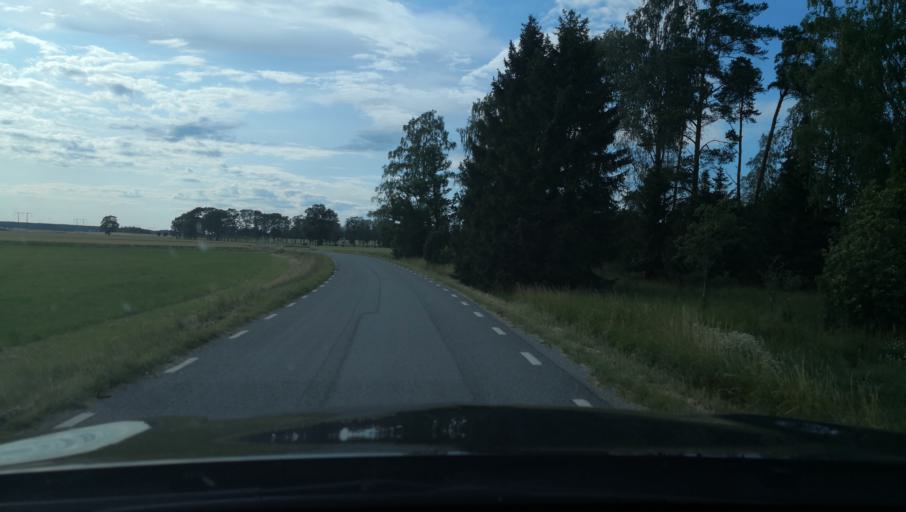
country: SE
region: Uppsala
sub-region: Enkopings Kommun
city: Orsundsbro
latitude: 59.6952
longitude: 17.3294
